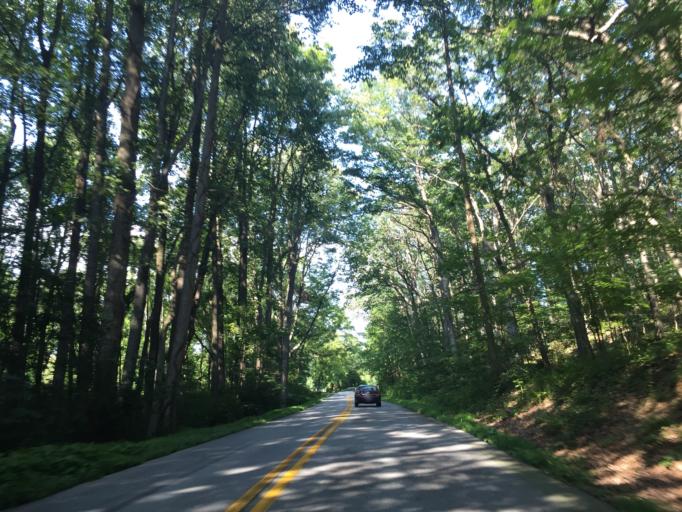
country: US
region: Maryland
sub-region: Carroll County
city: Manchester
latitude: 39.6302
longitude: -76.8895
